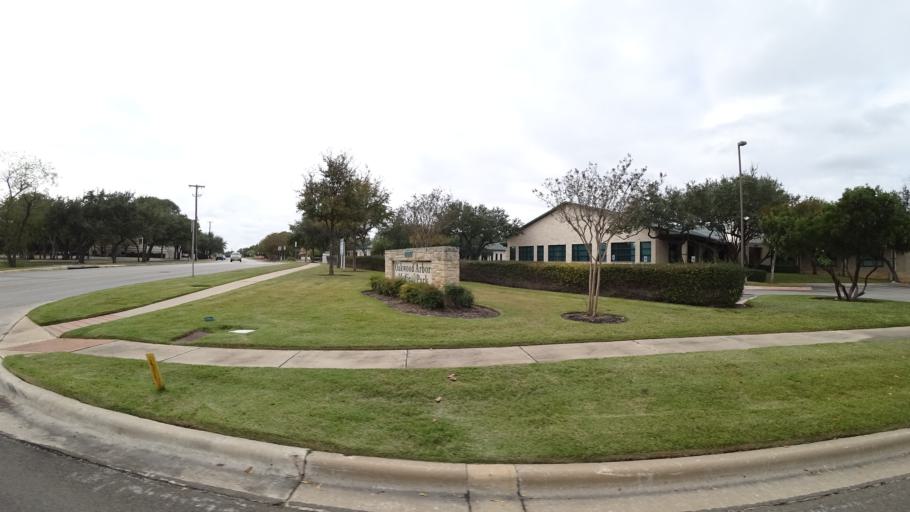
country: US
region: Texas
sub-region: Williamson County
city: Brushy Creek
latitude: 30.5130
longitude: -97.7105
